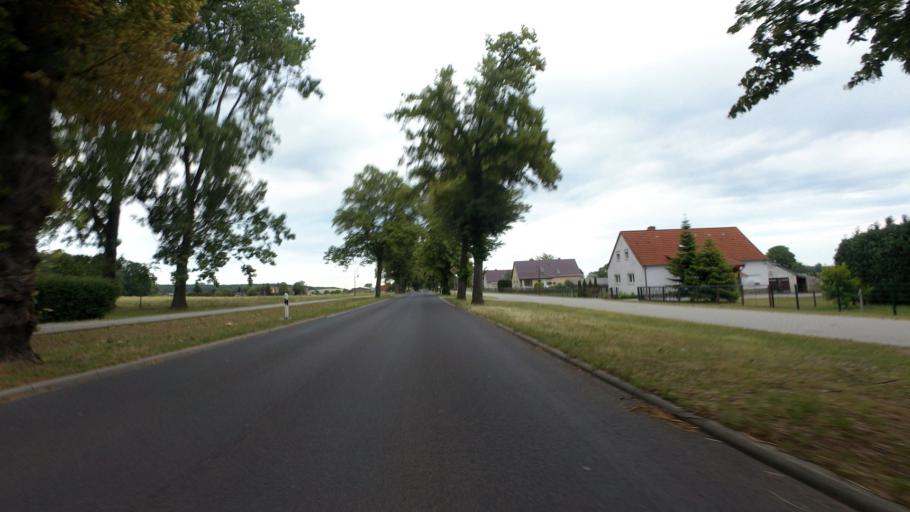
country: DE
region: Brandenburg
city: Roskow
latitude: 52.4808
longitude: 12.7744
